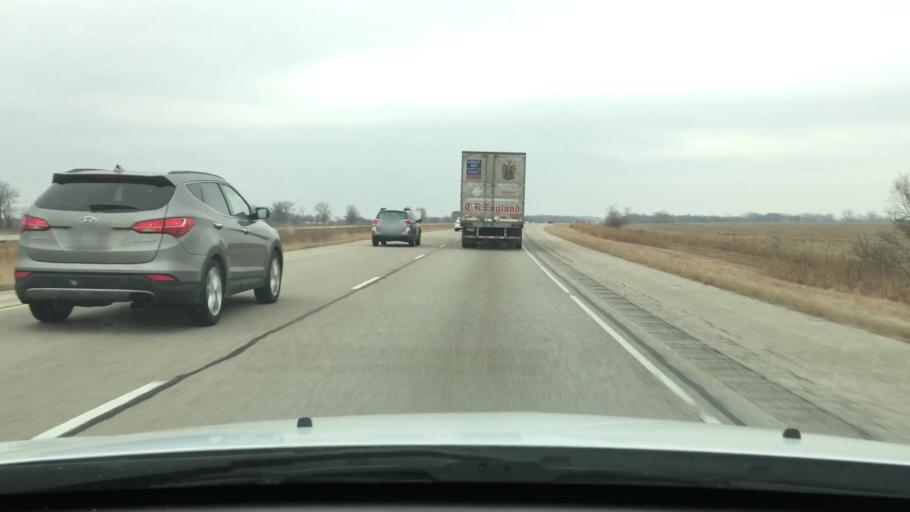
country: US
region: Illinois
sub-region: Logan County
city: Atlanta
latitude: 40.3268
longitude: -89.1536
